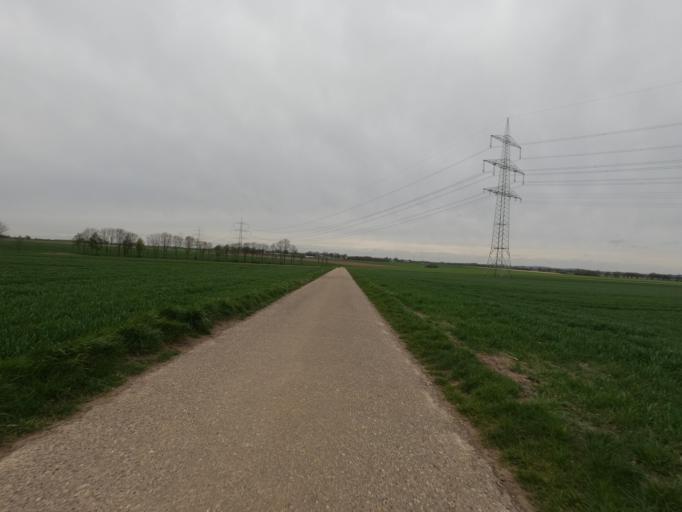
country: DE
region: North Rhine-Westphalia
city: Baesweiler
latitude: 50.9548
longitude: 6.1789
